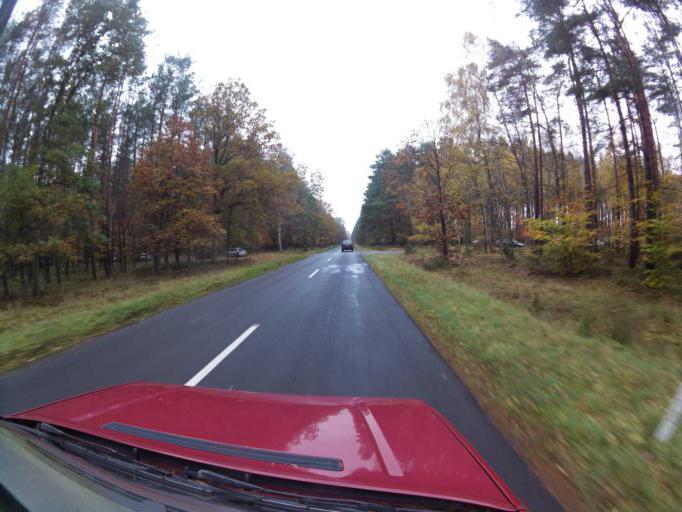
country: PL
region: West Pomeranian Voivodeship
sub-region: Powiat policki
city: Dobra
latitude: 53.5700
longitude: 14.4367
